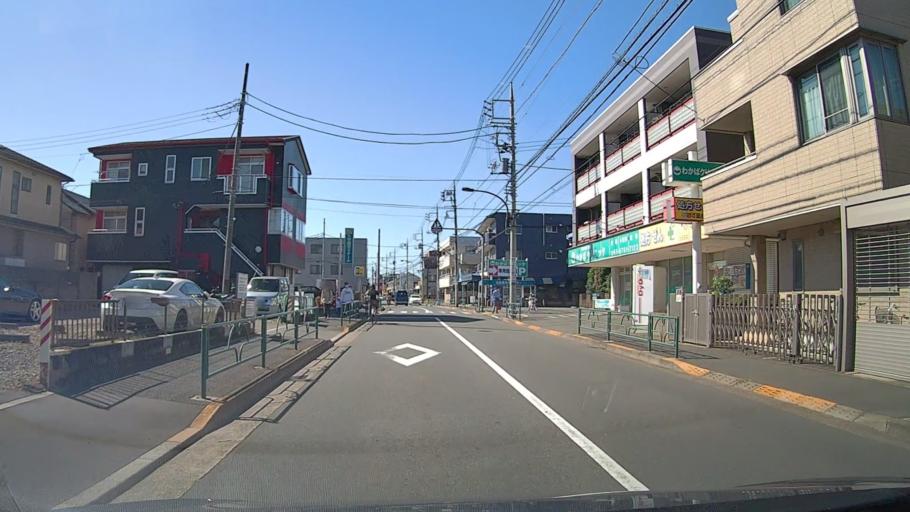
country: JP
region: Saitama
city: Wako
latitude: 35.7664
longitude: 139.6165
